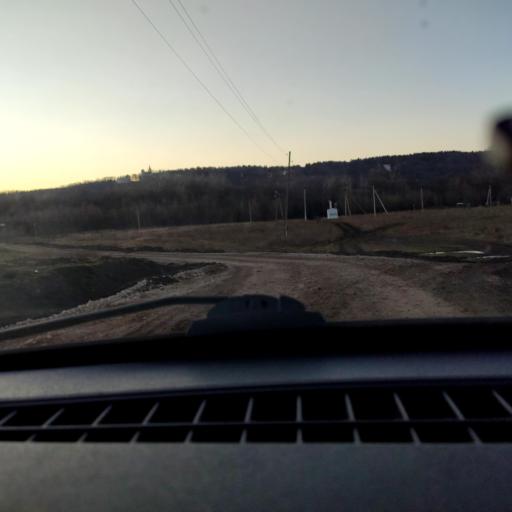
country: RU
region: Bashkortostan
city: Ufa
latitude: 54.7372
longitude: 56.0468
